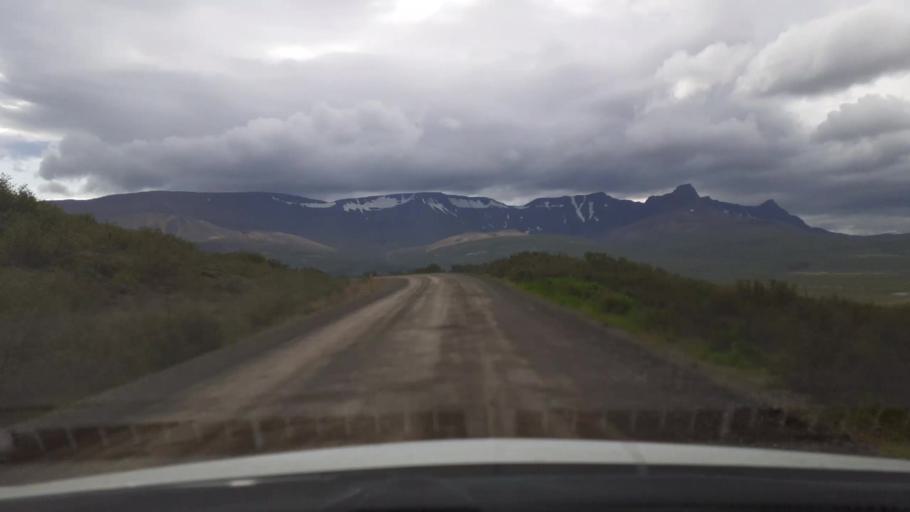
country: IS
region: West
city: Borgarnes
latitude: 64.5541
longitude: -21.6239
